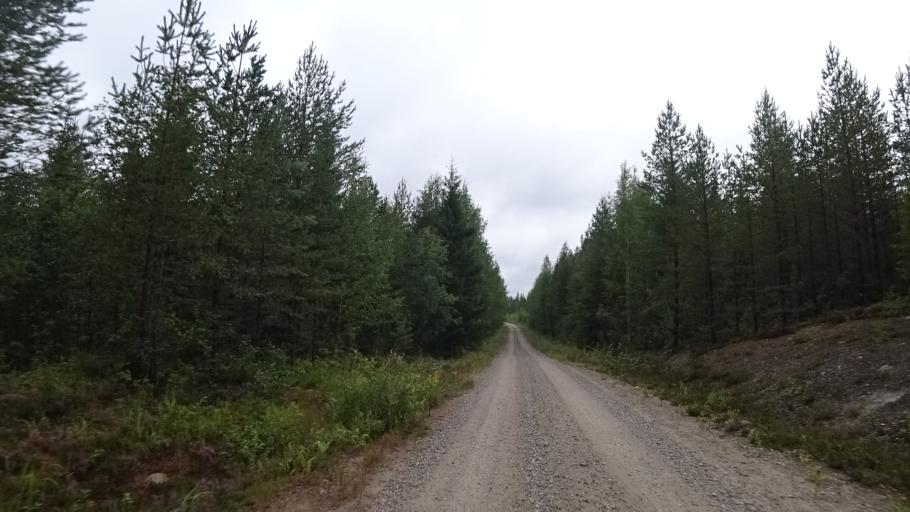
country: FI
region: North Karelia
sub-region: Pielisen Karjala
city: Lieksa
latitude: 63.5058
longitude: 30.1563
